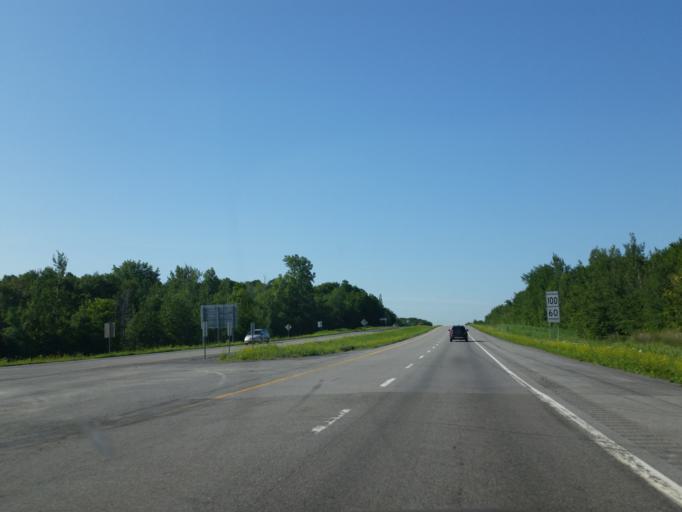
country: CA
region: Quebec
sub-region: Monteregie
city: Napierville
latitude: 45.2608
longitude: -73.4690
